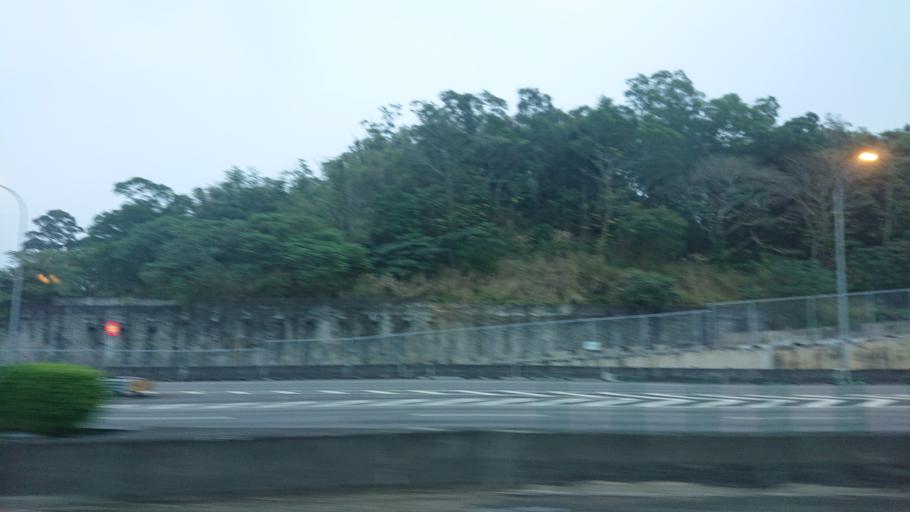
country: TW
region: Taiwan
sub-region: Miaoli
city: Miaoli
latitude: 24.5754
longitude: 120.8545
